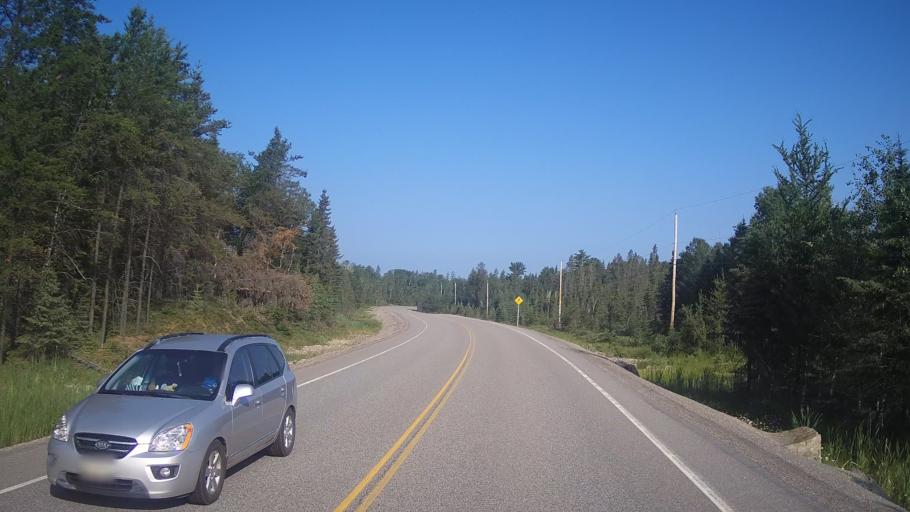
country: CA
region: Ontario
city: Rayside-Balfour
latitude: 46.7305
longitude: -81.5835
